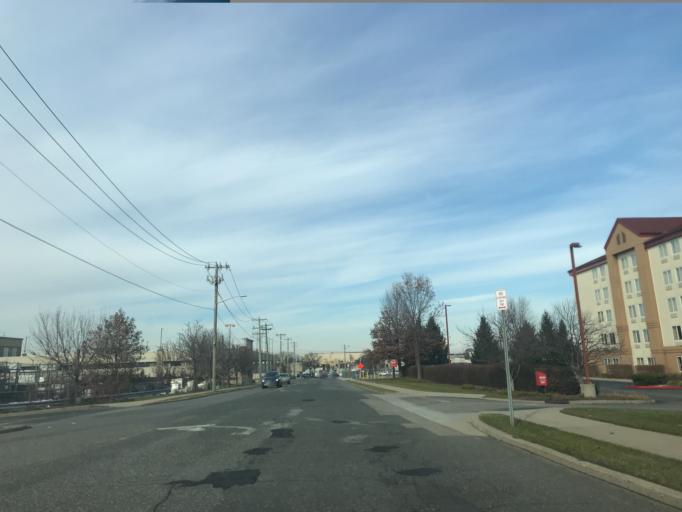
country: US
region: New York
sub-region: Nassau County
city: East Garden City
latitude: 40.7376
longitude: -73.6027
